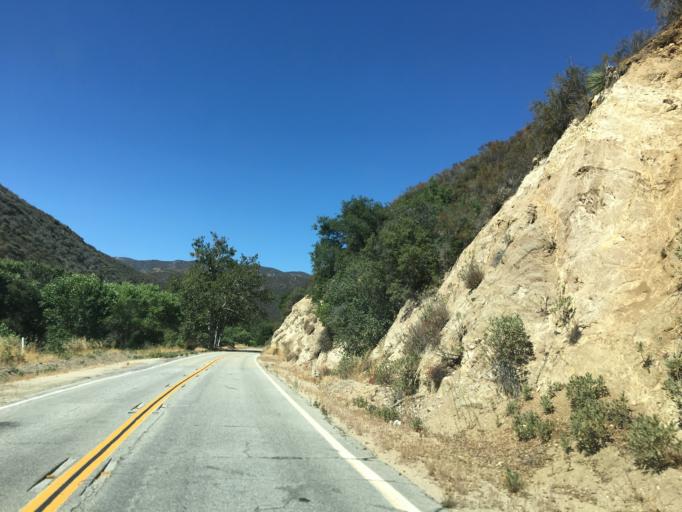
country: US
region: California
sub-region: Los Angeles County
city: Green Valley
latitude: 34.6253
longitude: -118.5510
